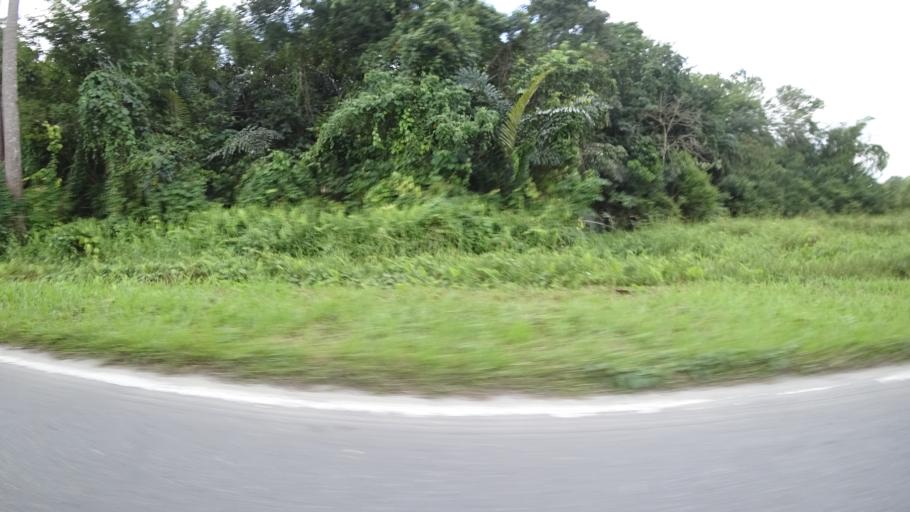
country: BN
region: Tutong
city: Tutong
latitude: 4.6979
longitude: 114.8034
